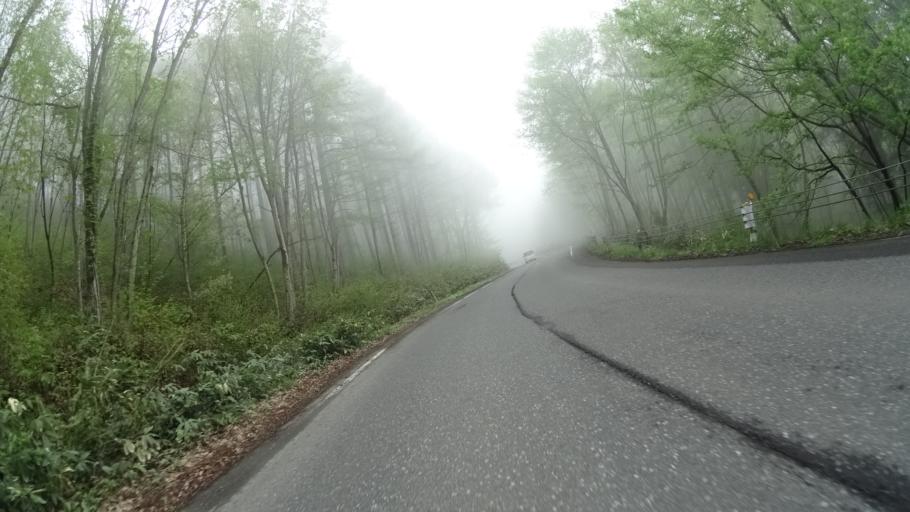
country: JP
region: Nagano
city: Nakano
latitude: 36.7186
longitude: 138.4507
